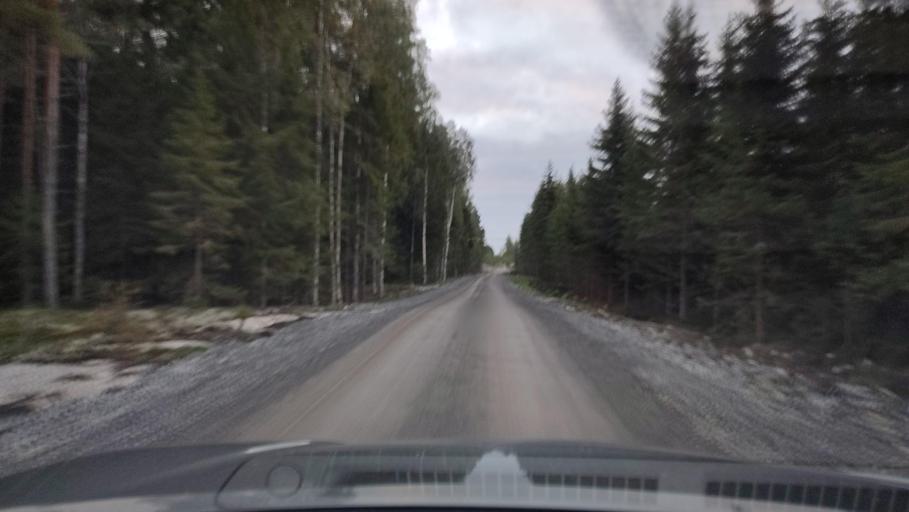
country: FI
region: Ostrobothnia
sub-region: Sydosterbotten
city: Kristinestad
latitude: 62.1903
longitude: 21.5329
